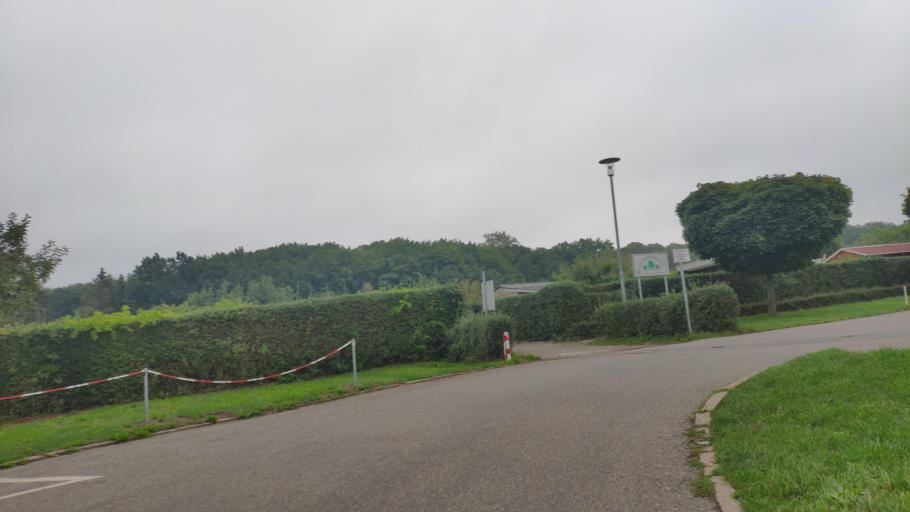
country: DE
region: Saxony
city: Hilbersdorf
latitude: 50.8349
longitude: 12.9685
